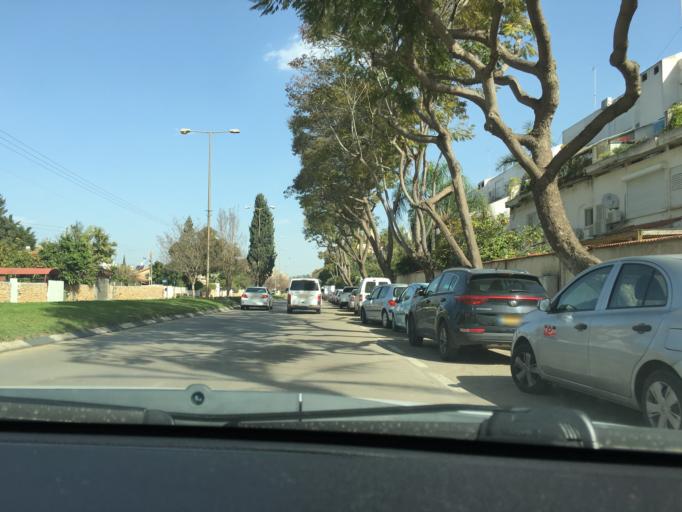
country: IL
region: Central District
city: Kfar Saba
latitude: 32.1829
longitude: 34.8998
